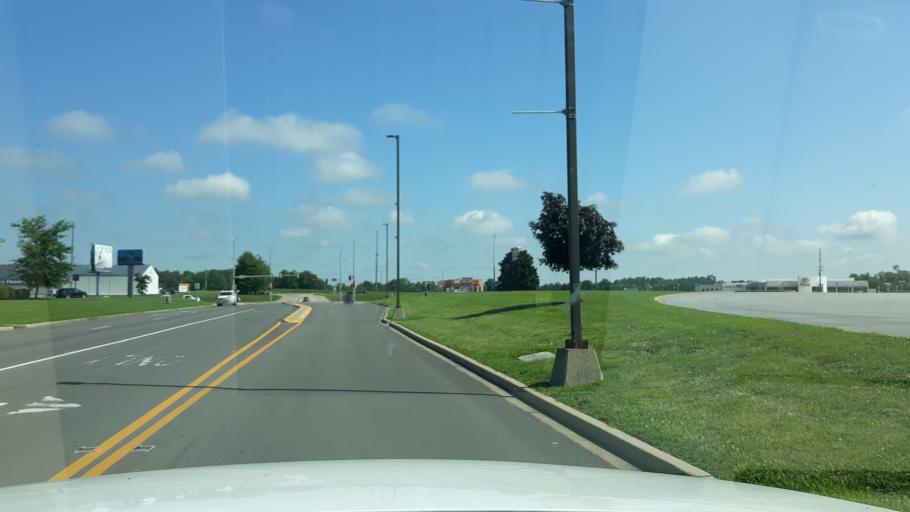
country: US
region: Illinois
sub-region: Williamson County
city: Energy
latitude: 37.7432
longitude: -88.9933
